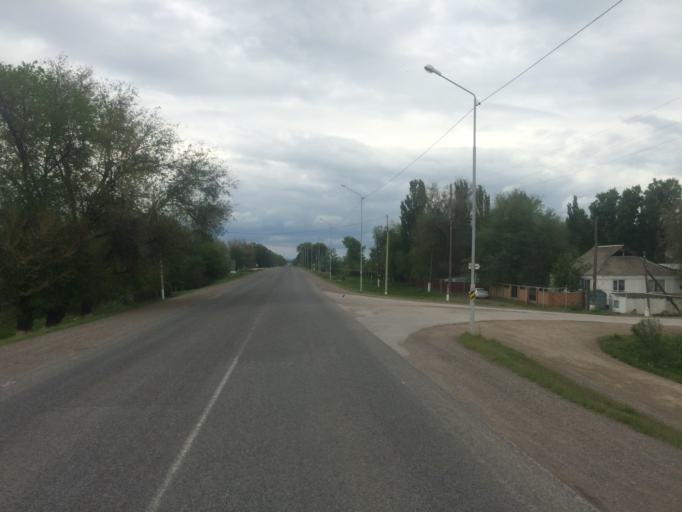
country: KZ
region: Zhambyl
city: Georgiyevka
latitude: 43.2267
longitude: 74.4006
